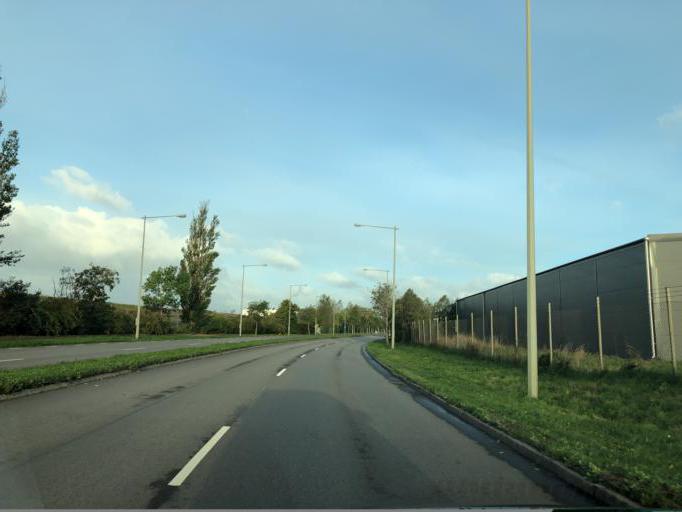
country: SE
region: Skane
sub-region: Landskrona
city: Landskrona
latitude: 55.8646
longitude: 12.8652
